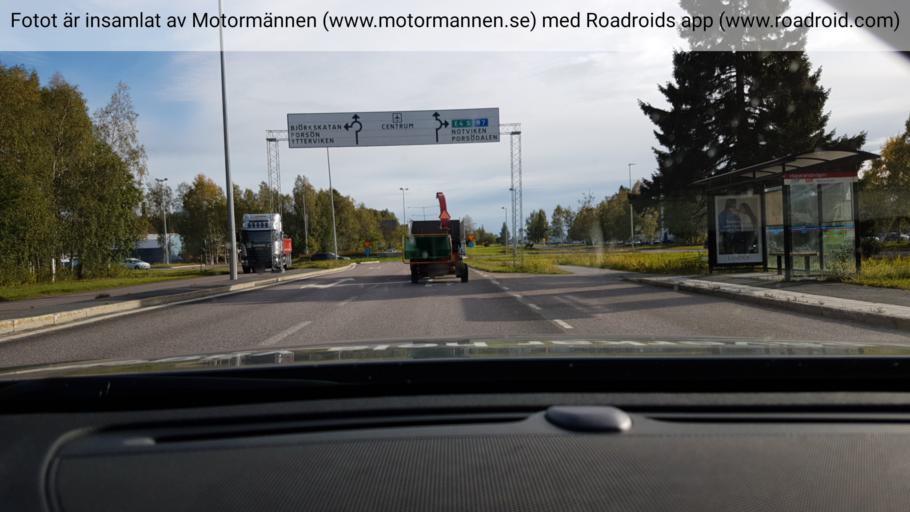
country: SE
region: Norrbotten
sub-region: Lulea Kommun
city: Lulea
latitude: 65.6138
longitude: 22.1334
